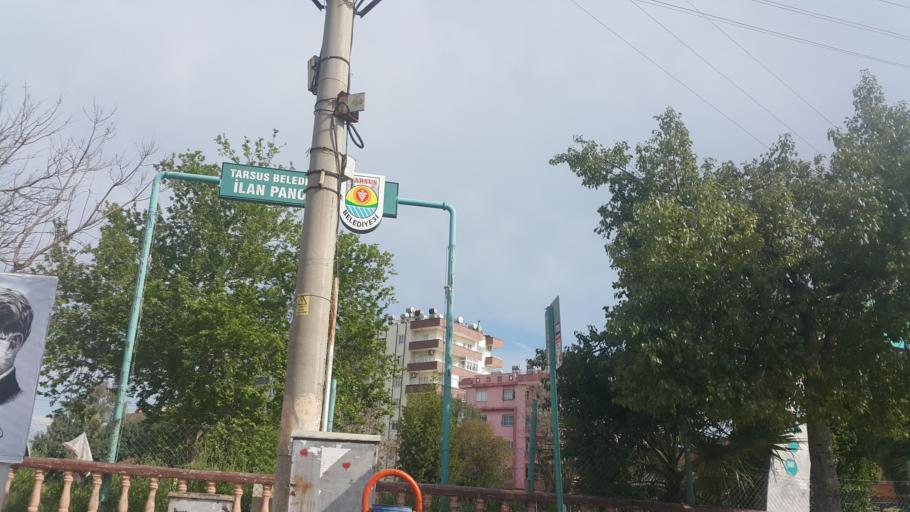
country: TR
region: Mersin
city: Tarsus
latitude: 36.9123
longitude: 34.8915
